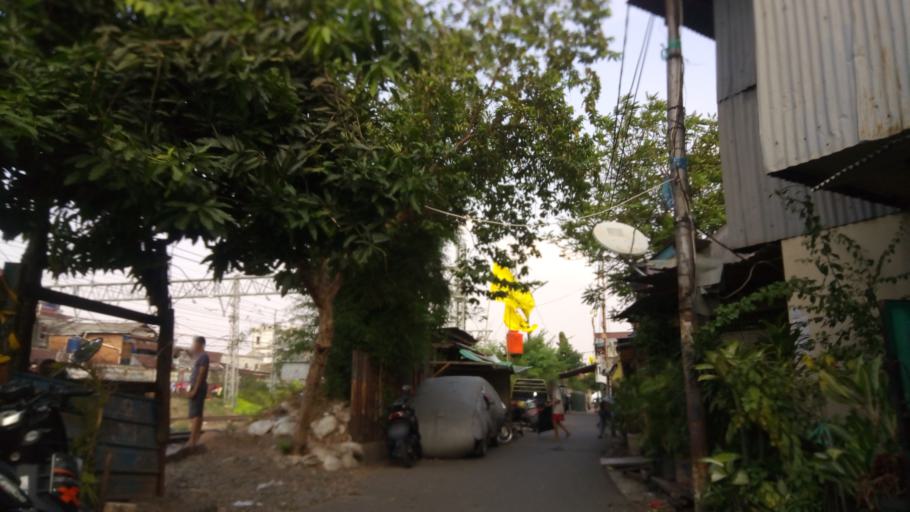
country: ID
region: Jakarta Raya
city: Jakarta
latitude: -6.2062
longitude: 106.8462
